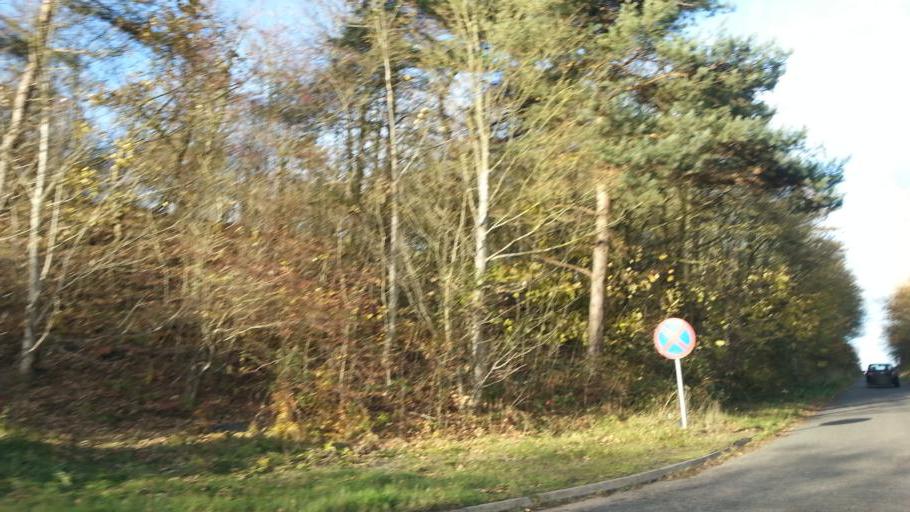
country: GB
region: England
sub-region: Leicestershire
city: Queniborough
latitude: 52.7220
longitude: -1.0756
